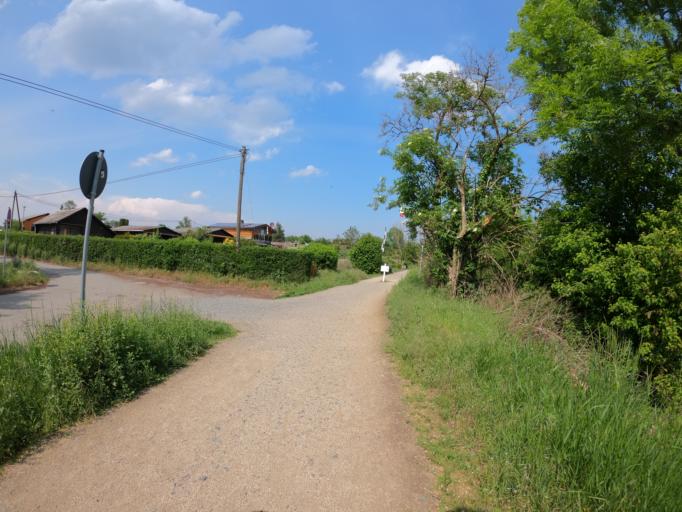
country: DE
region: Hesse
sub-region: Regierungsbezirk Darmstadt
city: Nauheim
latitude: 49.9481
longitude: 8.4720
